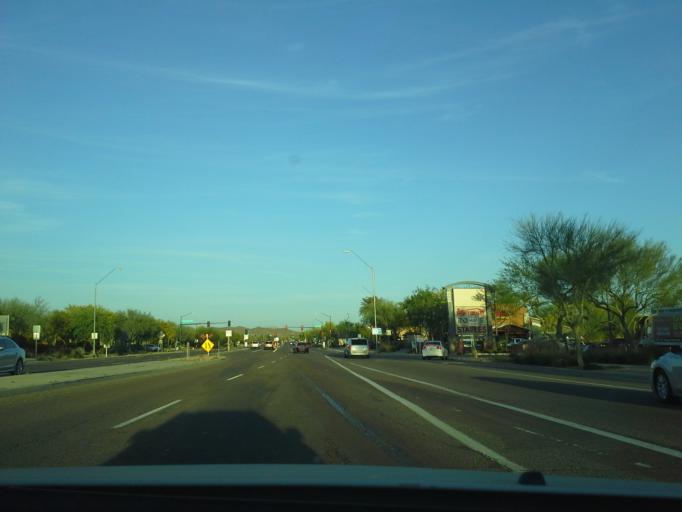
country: US
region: Arizona
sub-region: Maricopa County
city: Anthem
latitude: 33.7128
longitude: -112.1138
